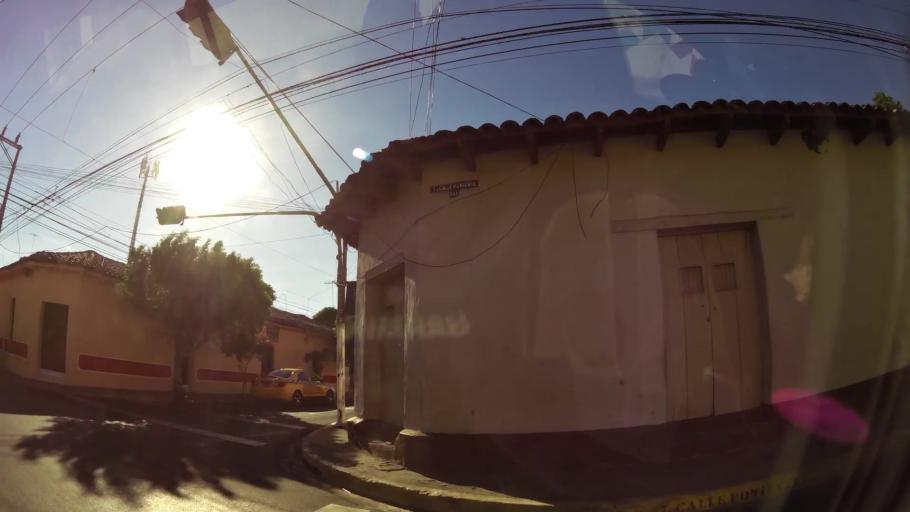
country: SV
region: San Miguel
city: San Miguel
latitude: 13.4766
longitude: -88.1803
